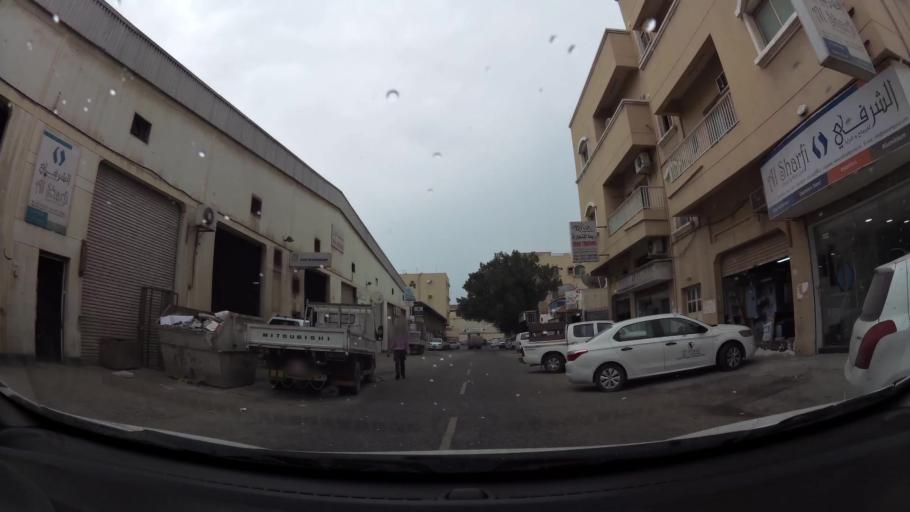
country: BH
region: Northern
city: Madinat `Isa
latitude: 26.1819
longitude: 50.5325
